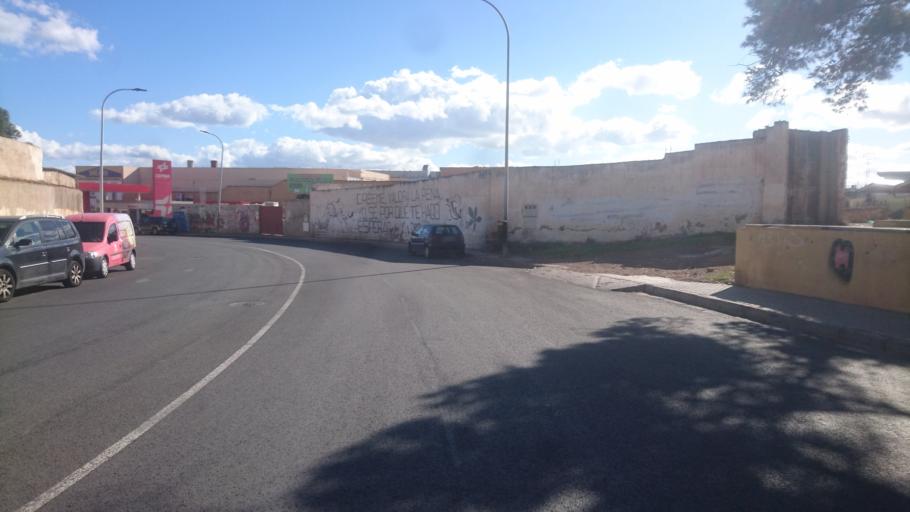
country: ES
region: Melilla
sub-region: Melilla
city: Melilla
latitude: 35.2725
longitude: -2.9465
